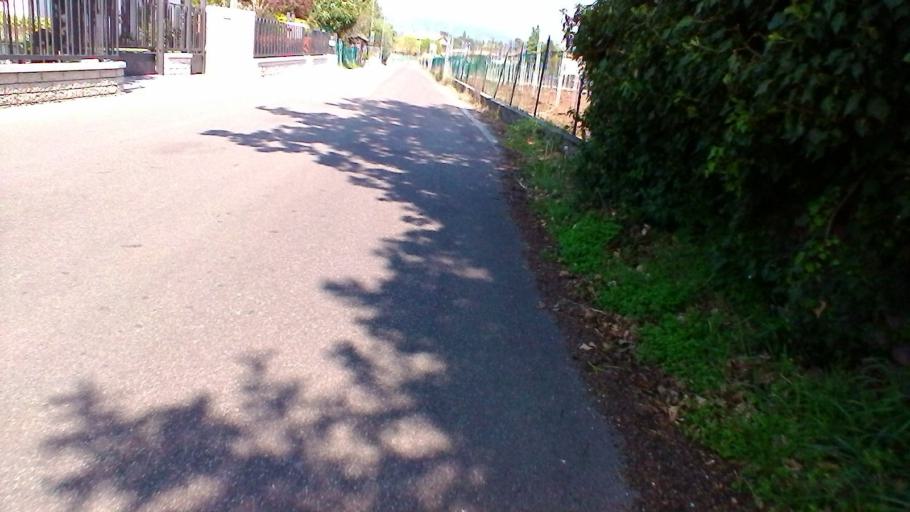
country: IT
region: Veneto
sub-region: Provincia di Verona
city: Parona
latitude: 45.4549
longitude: 10.9324
